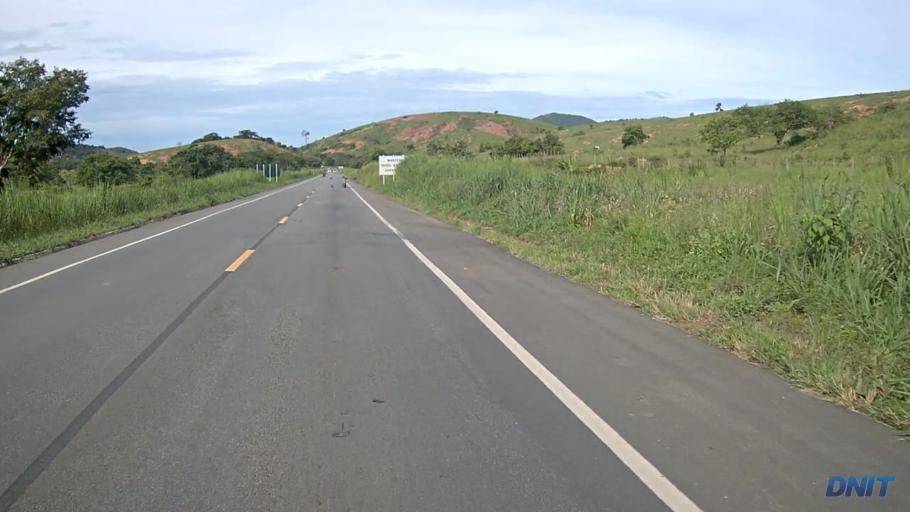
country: BR
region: Minas Gerais
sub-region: Belo Oriente
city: Belo Oriente
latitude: -19.2065
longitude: -42.2982
